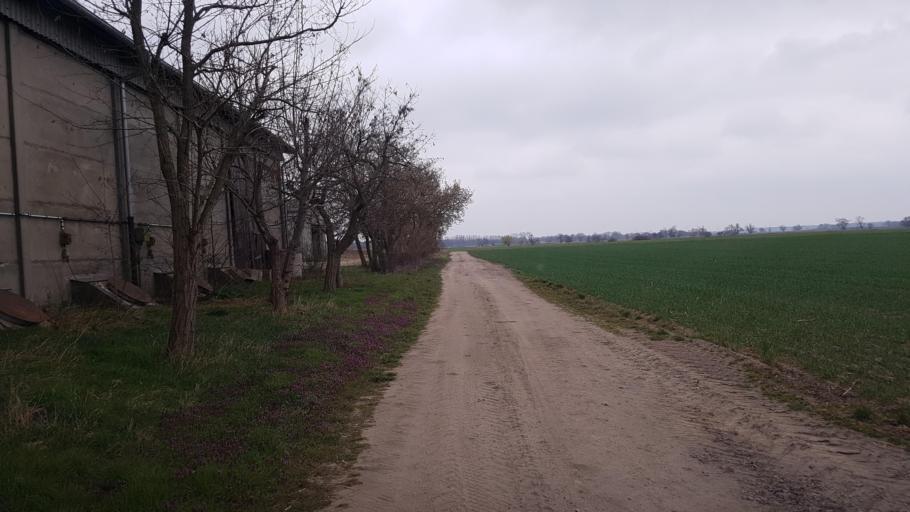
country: DE
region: Saxony
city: Nauwalde
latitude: 51.4406
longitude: 13.3650
